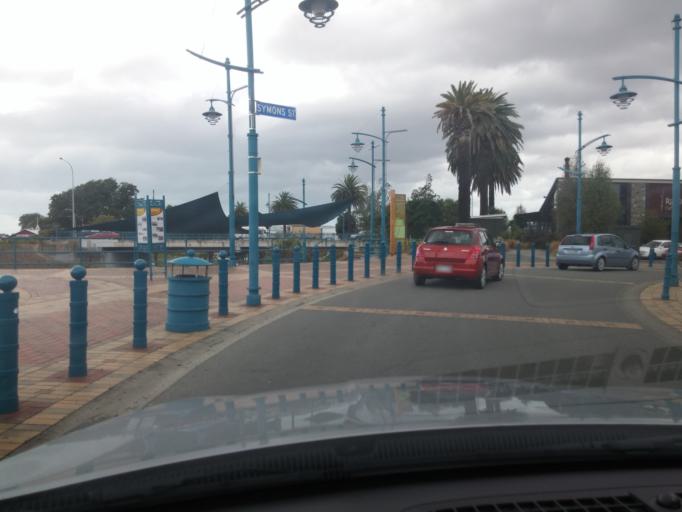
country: NZ
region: Marlborough
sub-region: Marlborough District
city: Blenheim
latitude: -41.5121
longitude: 173.9584
